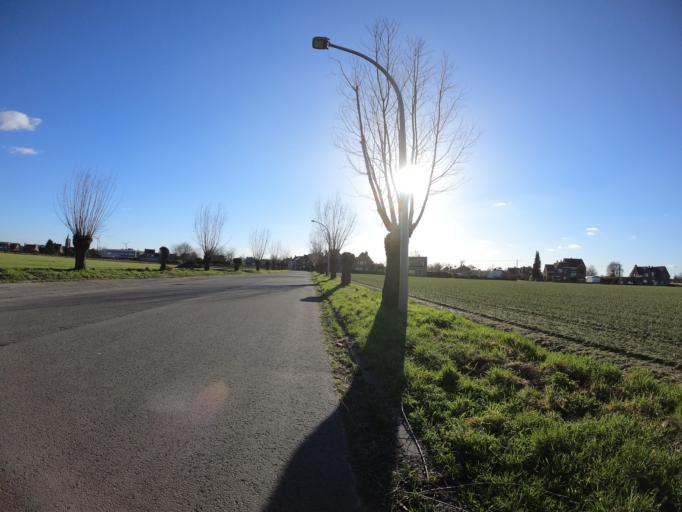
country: BE
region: Flanders
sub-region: Provincie West-Vlaanderen
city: Avelgem
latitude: 50.7821
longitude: 3.4451
